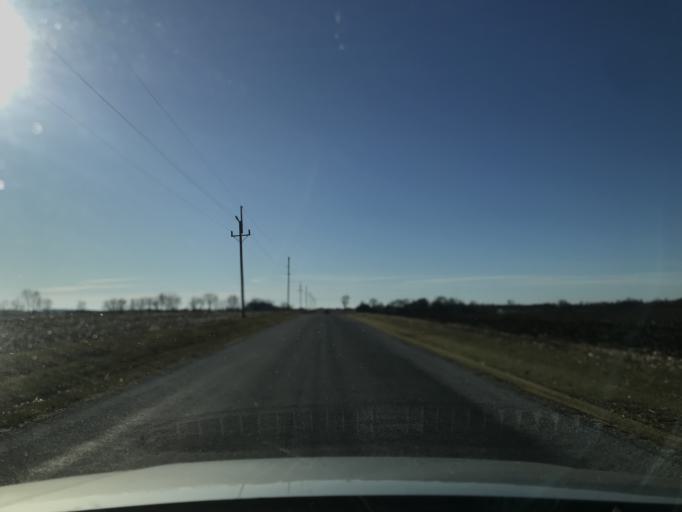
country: US
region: Illinois
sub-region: Hancock County
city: Carthage
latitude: 40.4672
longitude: -91.1784
